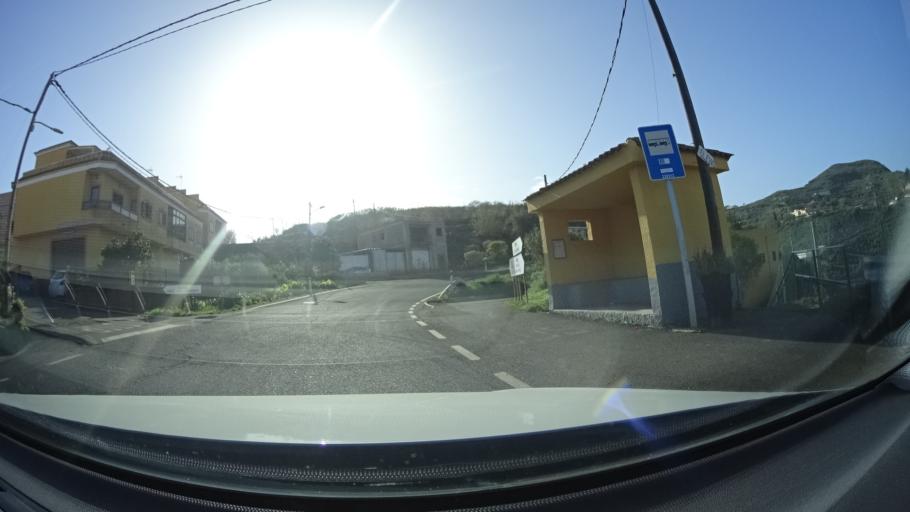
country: ES
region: Canary Islands
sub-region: Provincia de Las Palmas
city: Vega de San Mateo
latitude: 28.0256
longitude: -15.5459
